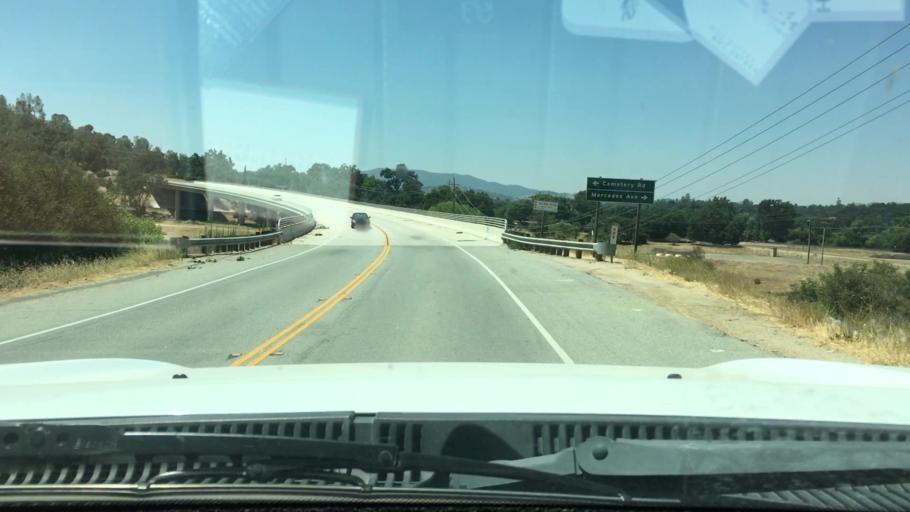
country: US
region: California
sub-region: San Luis Obispo County
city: Atascadero
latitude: 35.5022
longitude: -120.6573
